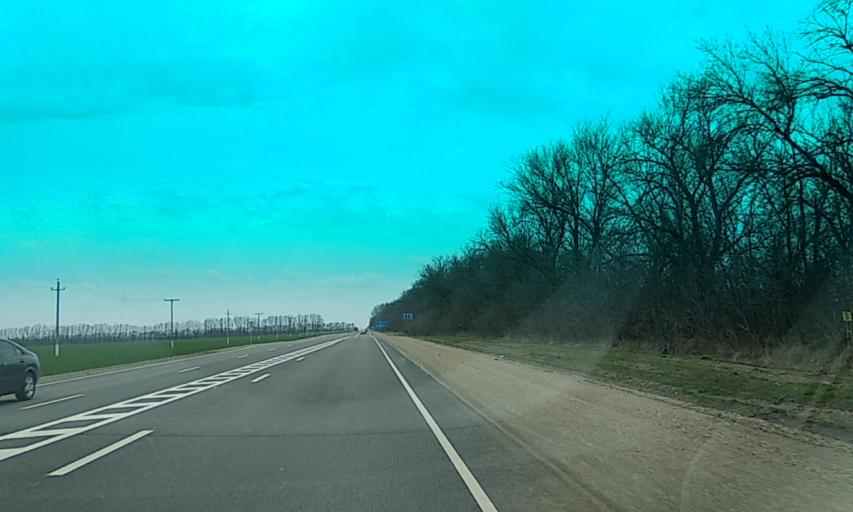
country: RU
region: Krasnodarskiy
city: Ust'-Labinsk
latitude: 45.3510
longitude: 39.6931
